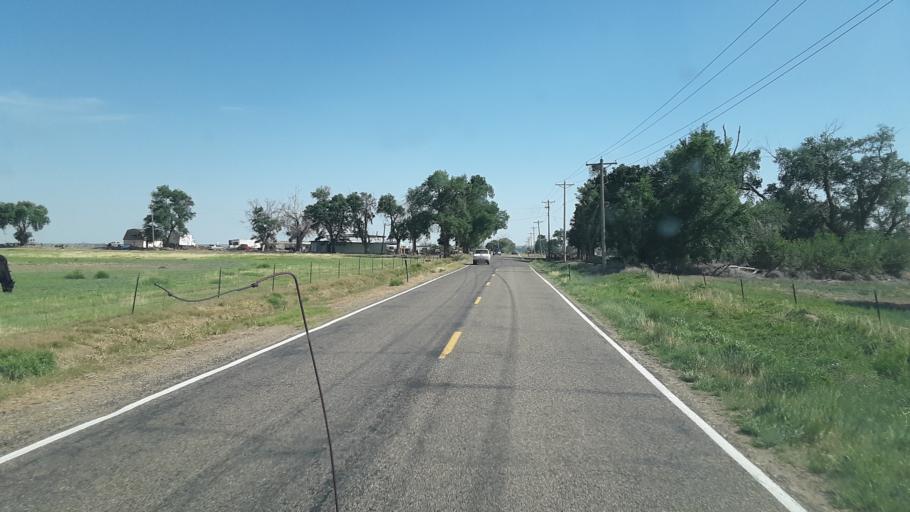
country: US
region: Colorado
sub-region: Crowley County
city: Ordway
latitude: 38.1573
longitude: -103.8570
